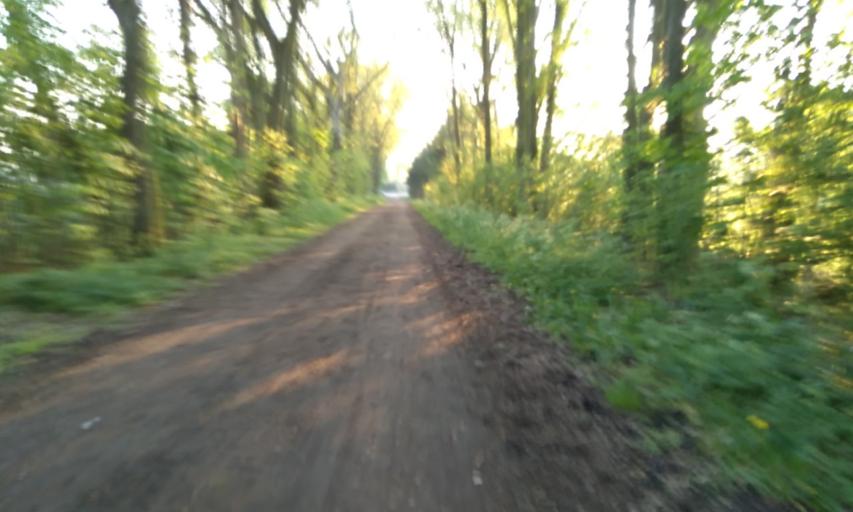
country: DE
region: Lower Saxony
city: Deinste
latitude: 53.5113
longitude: 9.4834
